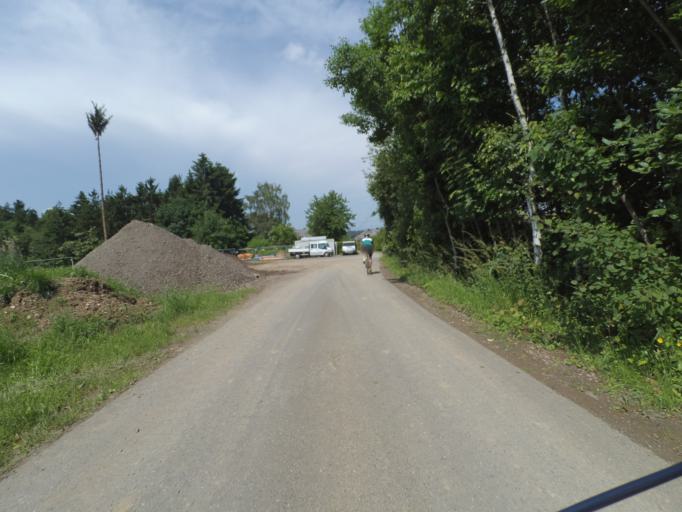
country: DE
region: Rheinland-Pfalz
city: Mermuth
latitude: 50.1679
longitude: 7.4820
